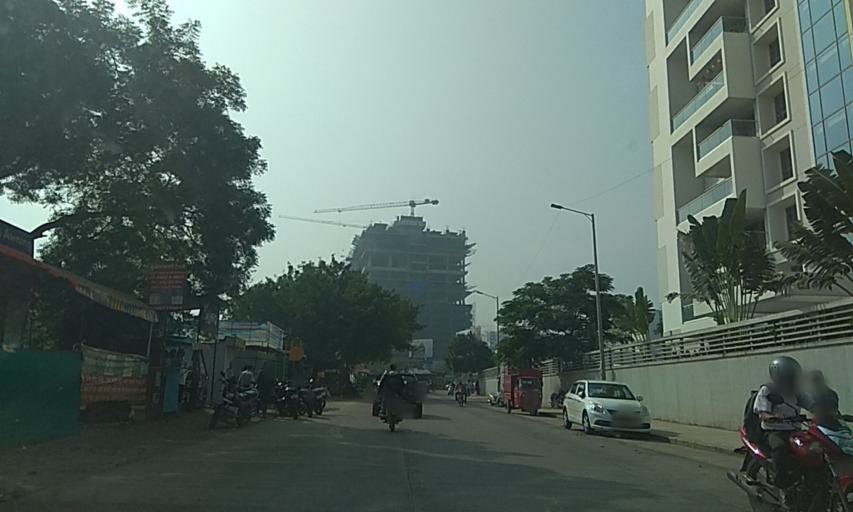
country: IN
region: Maharashtra
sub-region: Pune Division
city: Pimpri
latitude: 18.5595
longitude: 73.7765
